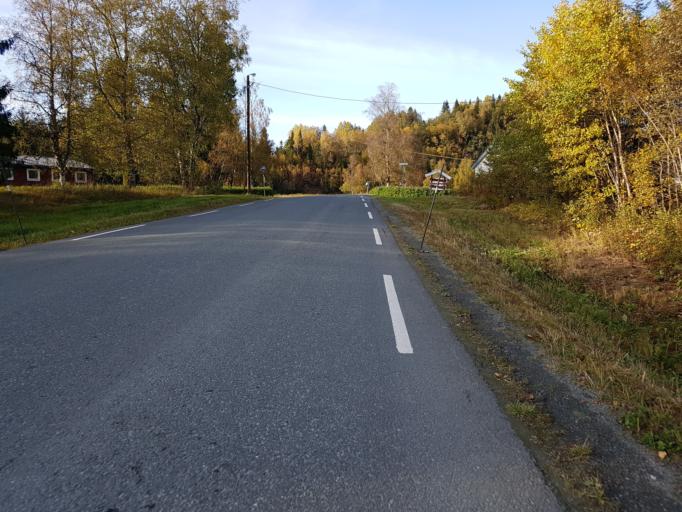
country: NO
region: Sor-Trondelag
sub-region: Klaebu
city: Klaebu
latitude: 63.3462
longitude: 10.5144
